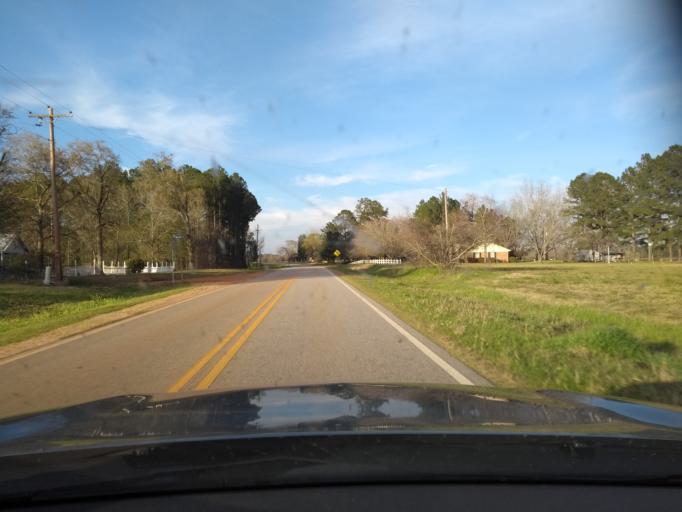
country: US
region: Georgia
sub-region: Bulloch County
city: Statesboro
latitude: 32.3212
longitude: -81.7771
